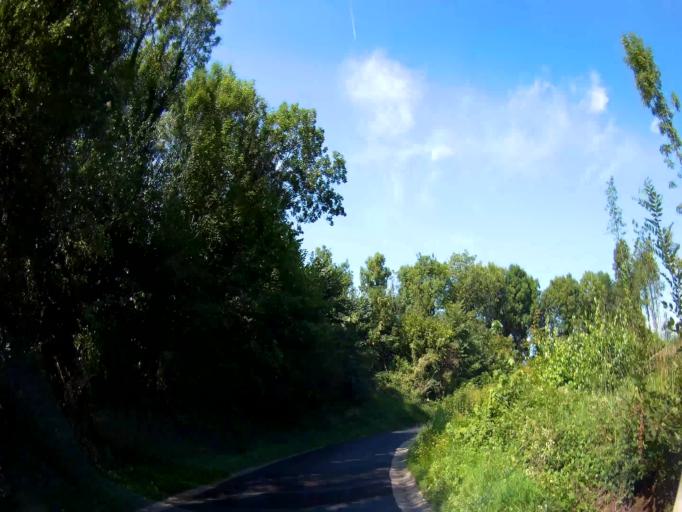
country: BE
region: Wallonia
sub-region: Province de Liege
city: Amay
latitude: 50.5693
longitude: 5.3308
